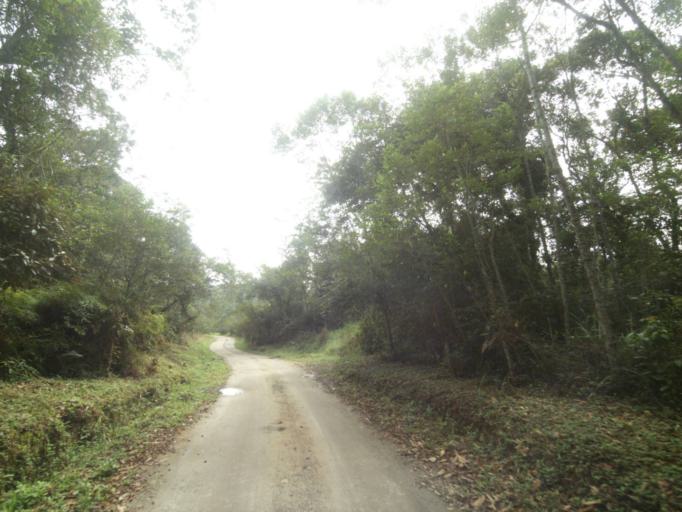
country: BR
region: Parana
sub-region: Paranagua
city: Paranagua
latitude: -25.5571
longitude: -48.6476
